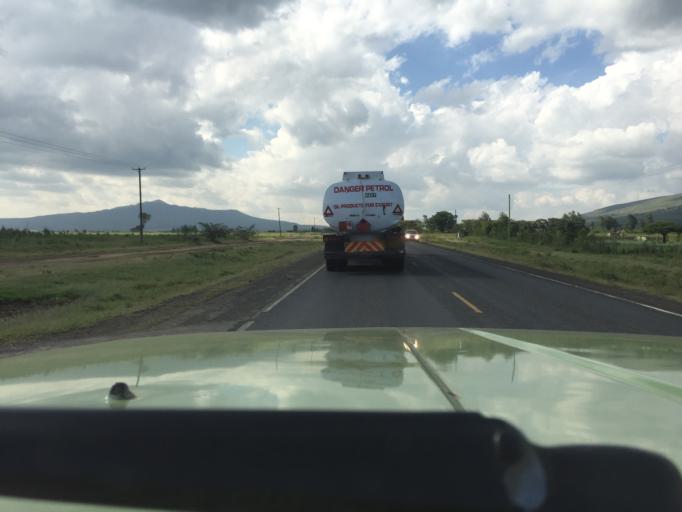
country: KE
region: Nakuru
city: Kijabe
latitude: -0.9578
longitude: 36.5564
